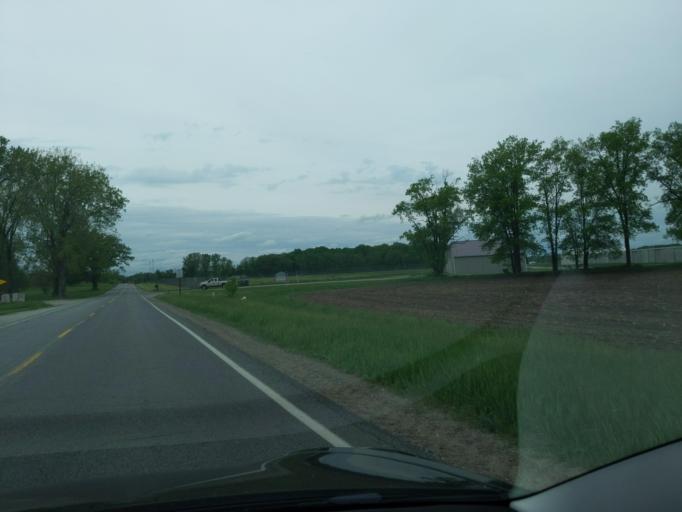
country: US
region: Michigan
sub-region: Ingham County
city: Mason
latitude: 42.5623
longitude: -84.4308
